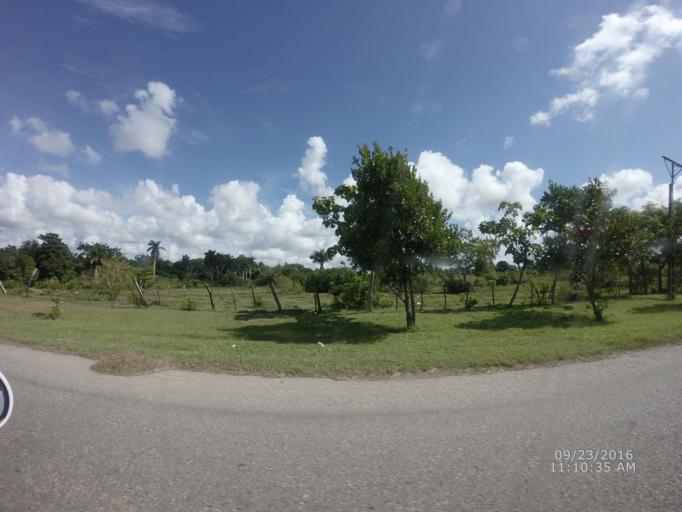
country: CU
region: La Habana
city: Arroyo Naranjo
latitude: 23.0213
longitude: -82.2579
